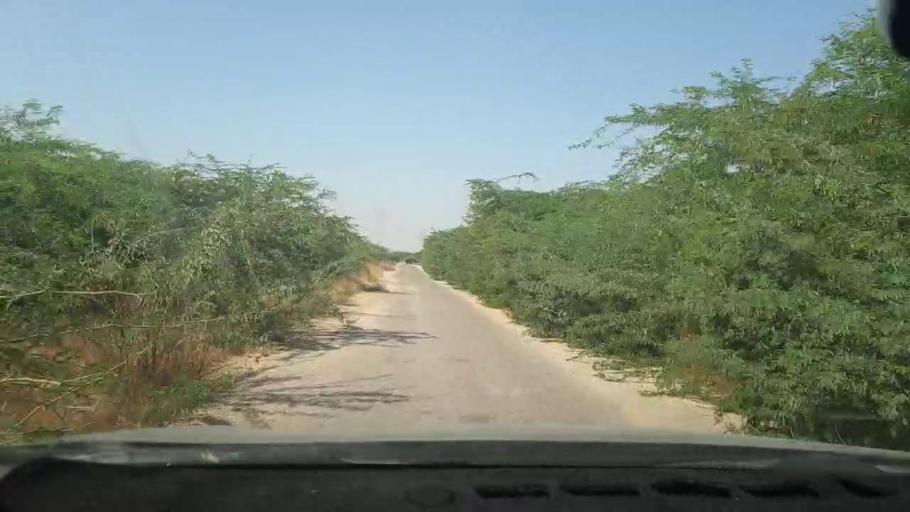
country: PK
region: Sindh
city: Malir Cantonment
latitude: 25.1568
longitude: 67.1440
